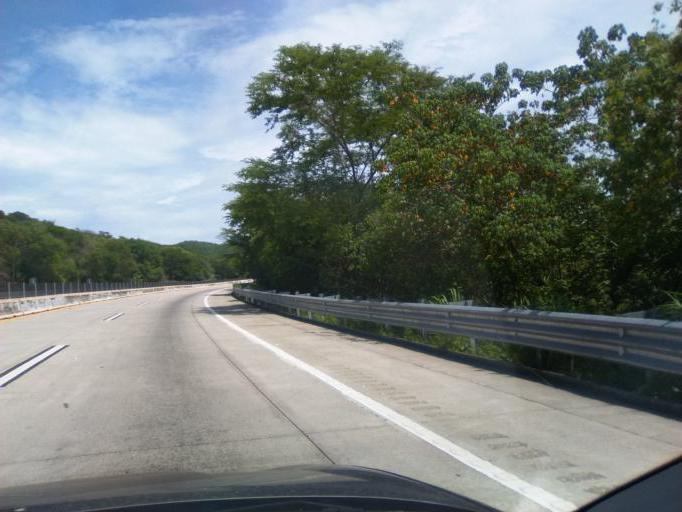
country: MX
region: Guerrero
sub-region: Acapulco de Juarez
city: Pueblo Madero (El Playon)
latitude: 17.0802
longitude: -99.6023
